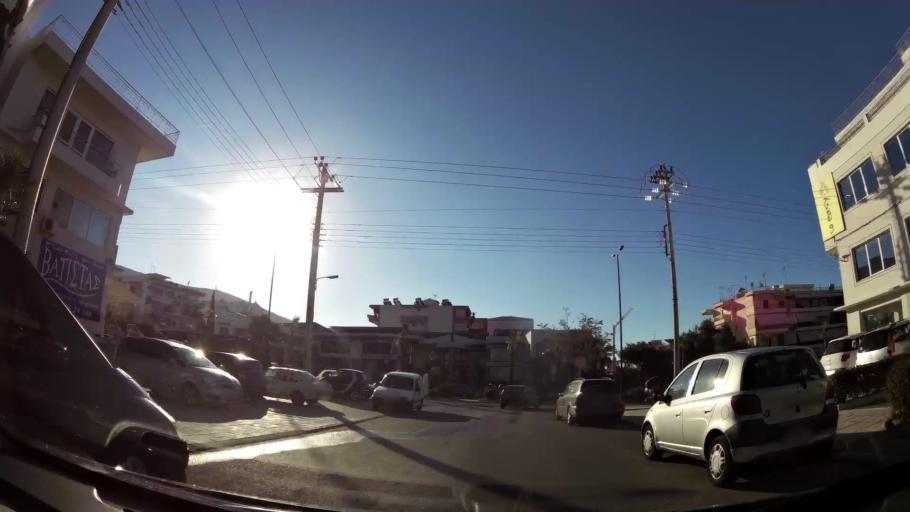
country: GR
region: Attica
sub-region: Nomarchia Athinas
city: Glyfada
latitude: 37.8735
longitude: 23.7634
